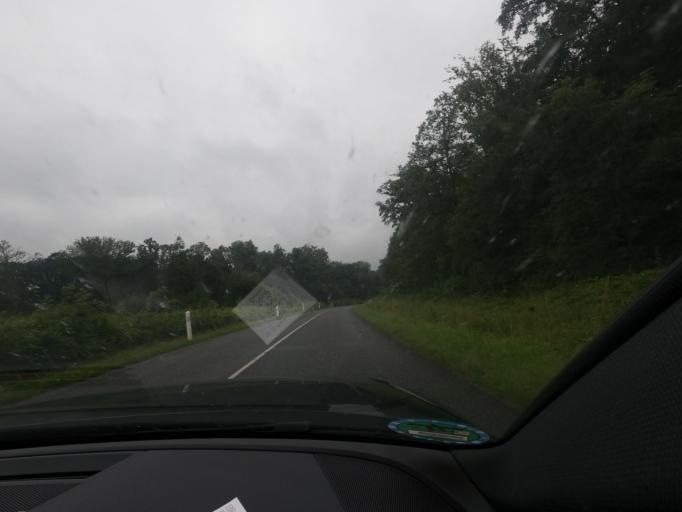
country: FR
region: Picardie
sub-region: Departement de l'Oise
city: Ressons-sur-Matz
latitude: 49.5263
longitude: 2.7167
